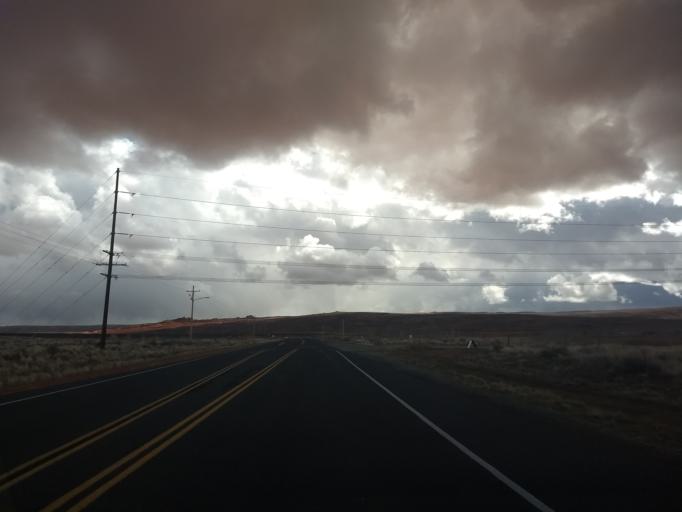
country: US
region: Utah
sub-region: Washington County
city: Hurricane
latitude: 37.1238
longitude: -113.3927
